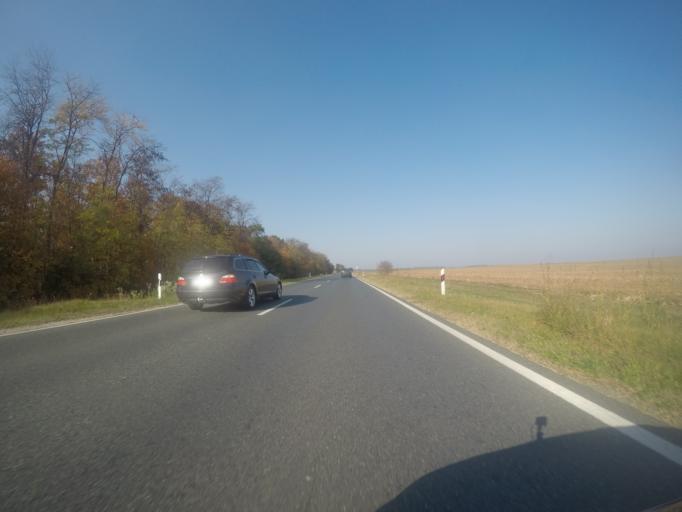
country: HU
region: Tolna
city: Madocsa
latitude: 46.7082
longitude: 18.8880
